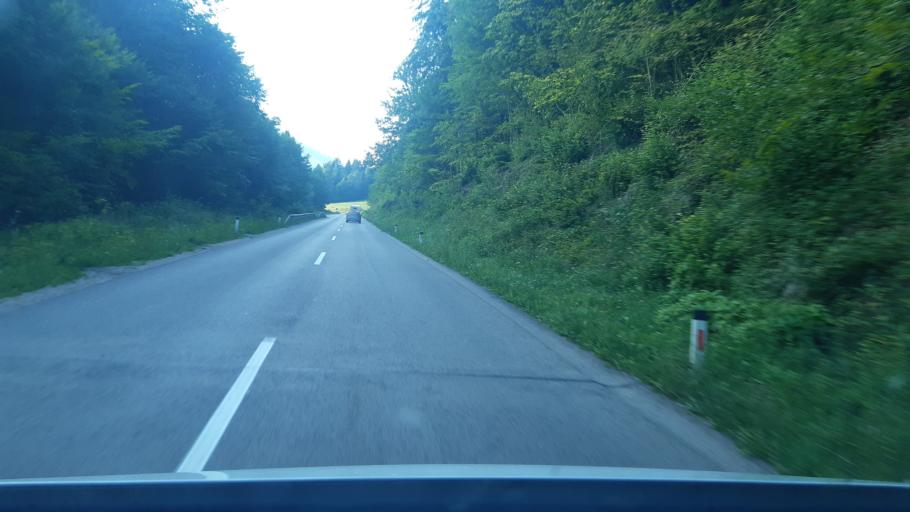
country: SI
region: Semic
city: Semic
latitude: 45.6592
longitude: 15.1157
